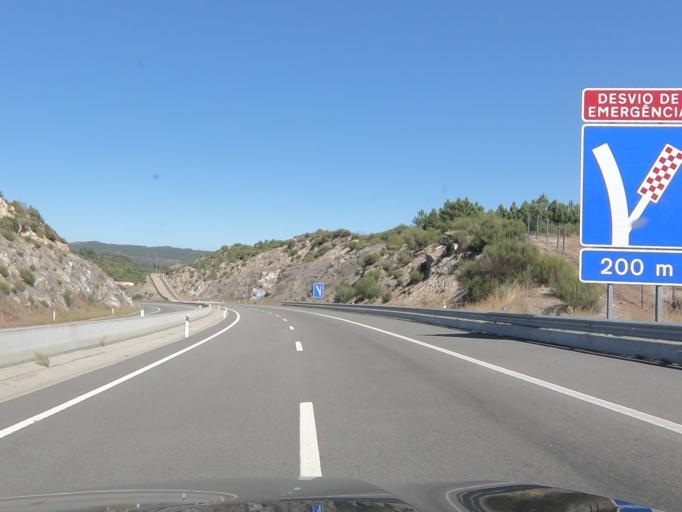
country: PT
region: Vila Real
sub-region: Murca
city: Murca
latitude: 41.3812
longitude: -7.4824
